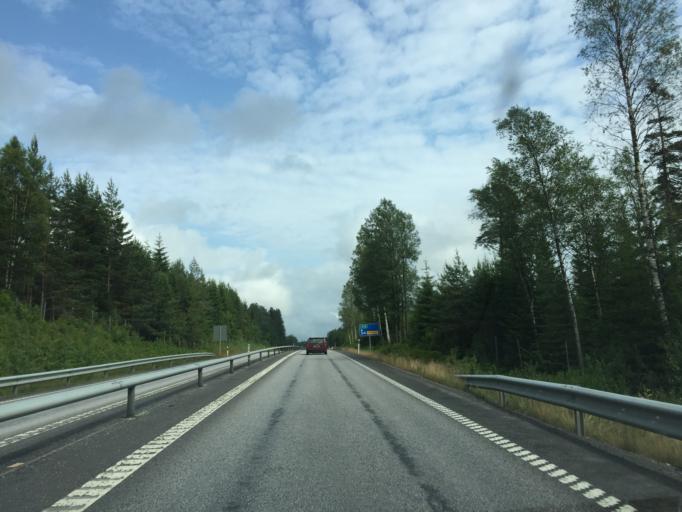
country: SE
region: OErebro
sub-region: Lekebergs Kommun
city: Fjugesta
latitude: 59.2773
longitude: 14.7293
